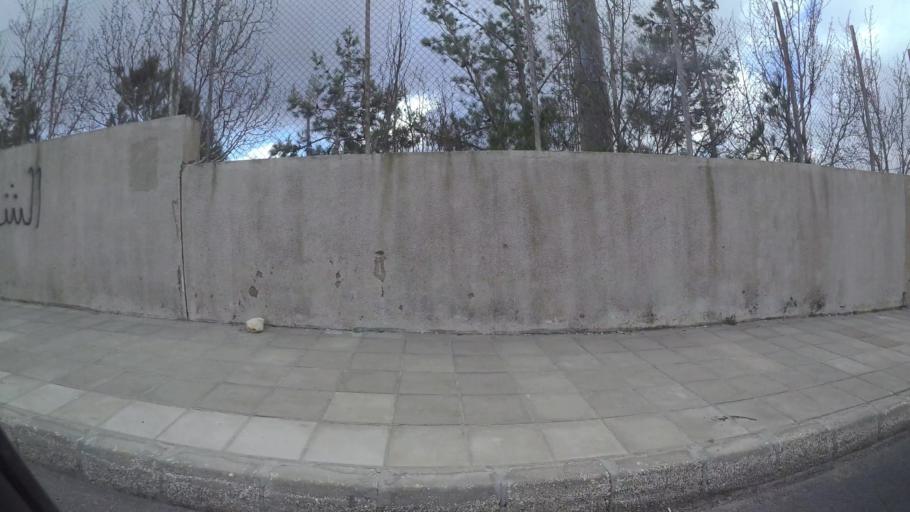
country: JO
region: Amman
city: Al Jubayhah
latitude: 32.0391
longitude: 35.8976
